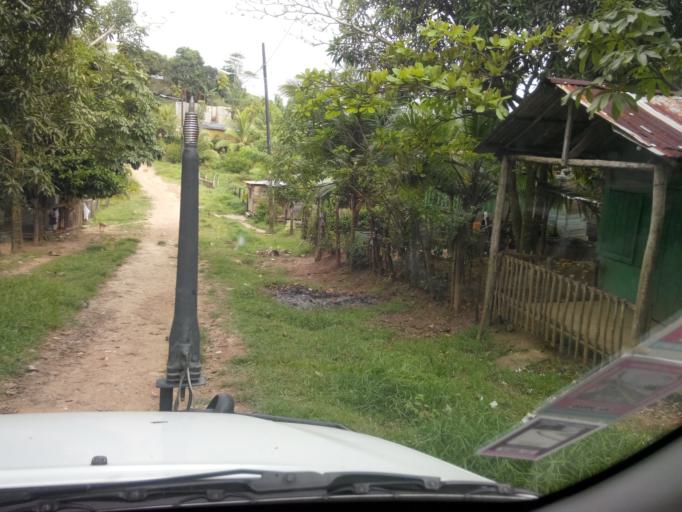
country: NI
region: Atlantico Sur
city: Bluefields
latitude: 12.0279
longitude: -83.7763
